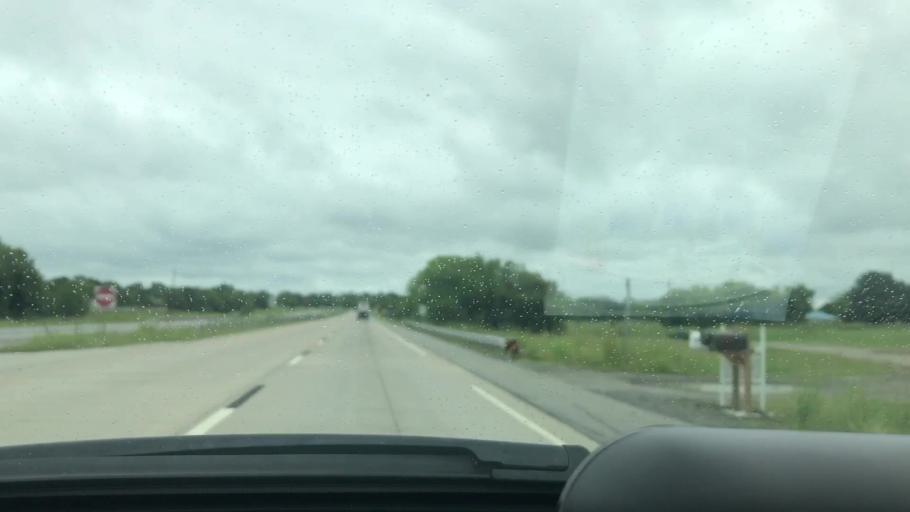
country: US
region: Oklahoma
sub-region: Pittsburg County
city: McAlester
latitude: 34.8185
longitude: -95.8533
